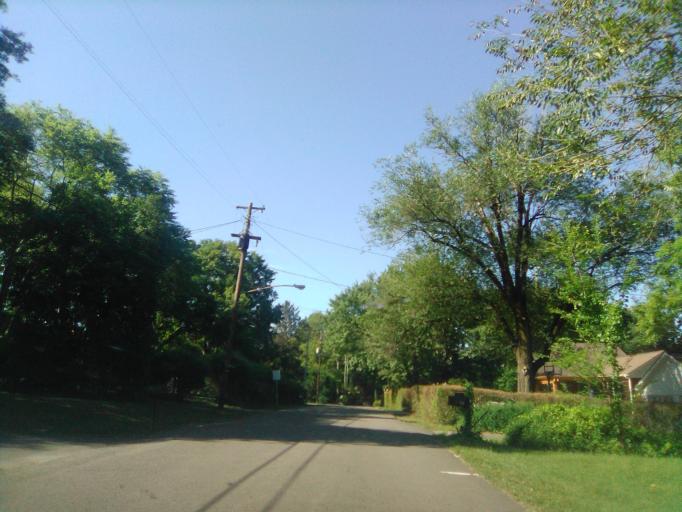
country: US
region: Tennessee
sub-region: Davidson County
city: Belle Meade
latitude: 36.1195
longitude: -86.8377
